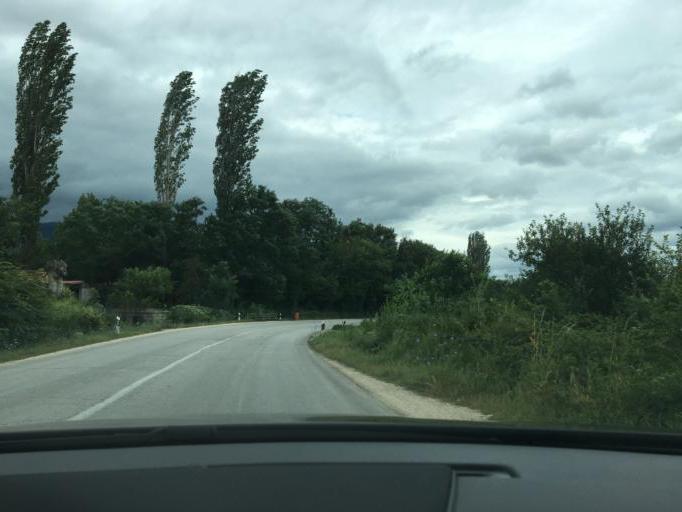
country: MK
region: Kriva Palanka
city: Kriva Palanka
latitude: 42.1774
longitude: 22.2600
